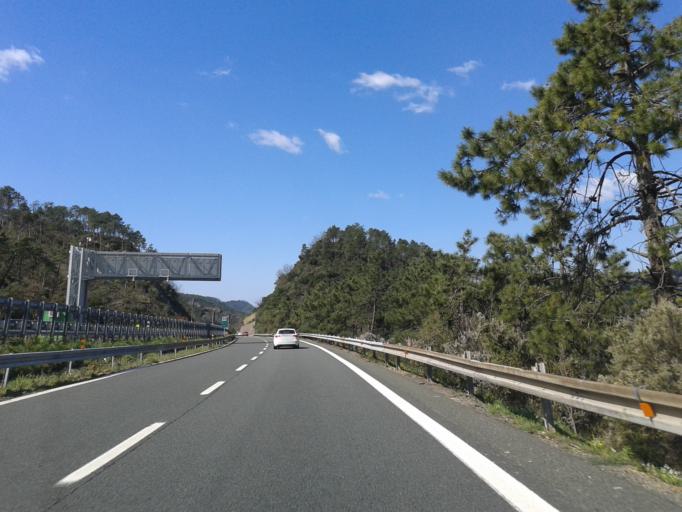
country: IT
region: Liguria
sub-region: Provincia di Genova
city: Casarza Ligure
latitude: 44.2712
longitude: 9.4677
